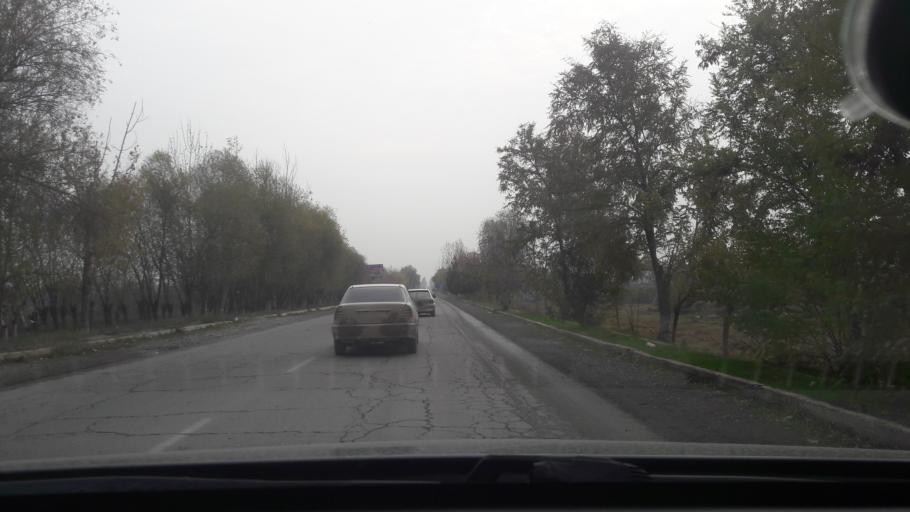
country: TJ
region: Khatlon
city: Qurghonteppa
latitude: 37.8659
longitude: 68.7157
